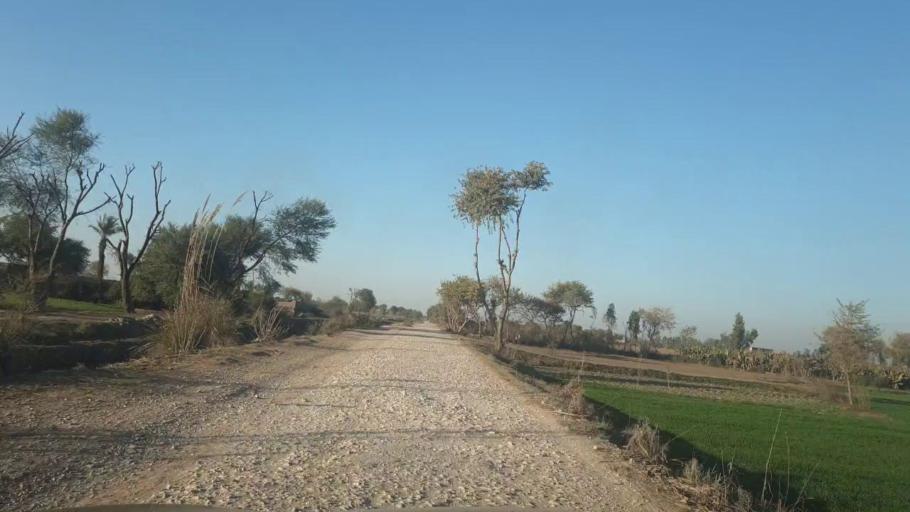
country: PK
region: Sindh
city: Ghotki
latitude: 27.9990
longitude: 69.2712
